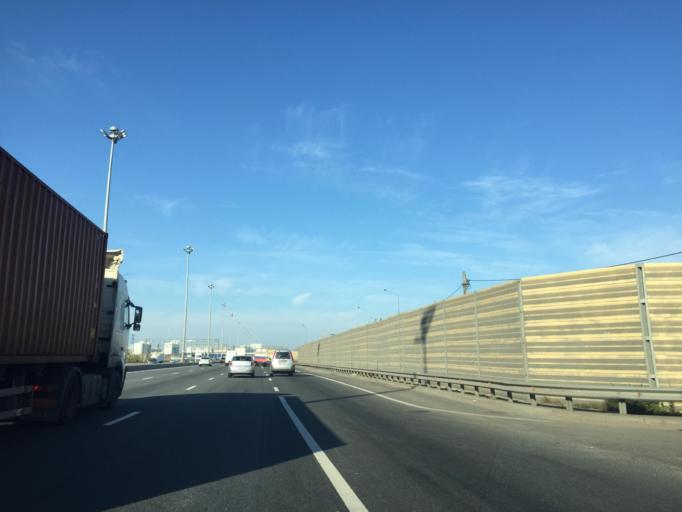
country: RU
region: St.-Petersburg
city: Petro-Slavyanka
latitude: 59.7476
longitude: 30.4992
